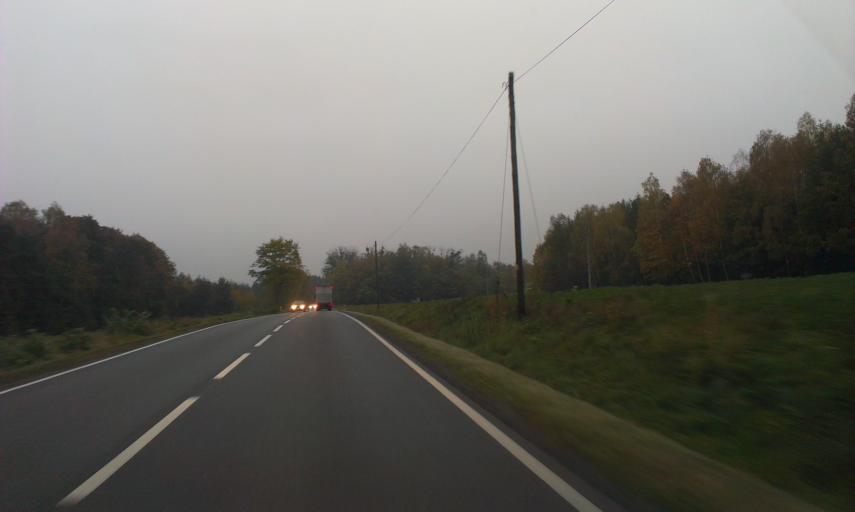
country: PL
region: Kujawsko-Pomorskie
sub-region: Powiat sepolenski
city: Sepolno Krajenskie
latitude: 53.4357
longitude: 17.5628
